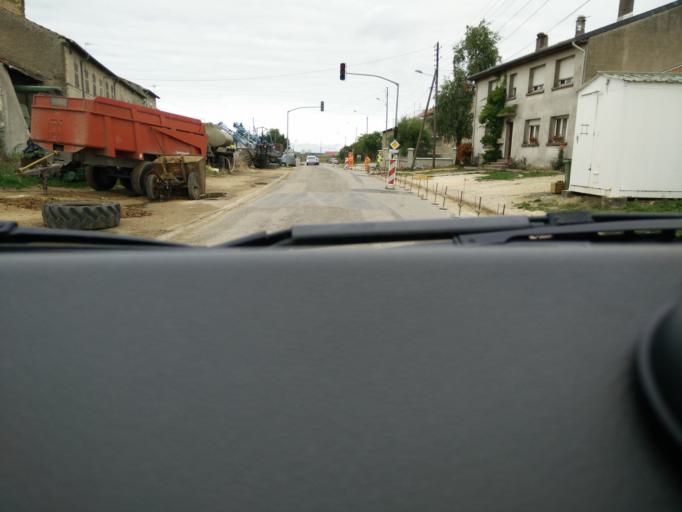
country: FR
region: Lorraine
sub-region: Departement de la Meuse
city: Vigneulles-les-Hattonchatel
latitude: 48.9631
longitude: 5.8238
